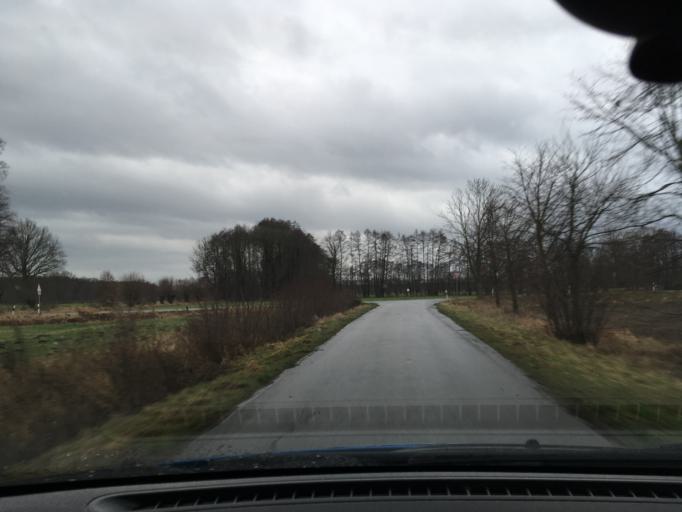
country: DE
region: Lower Saxony
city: Neetze
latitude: 53.3182
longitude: 10.6383
